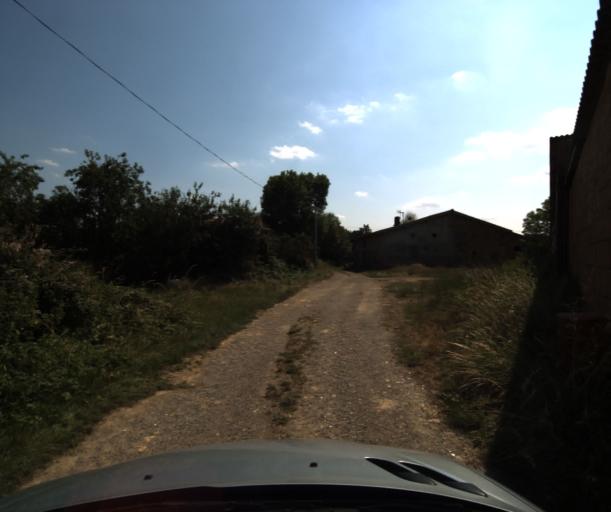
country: FR
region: Midi-Pyrenees
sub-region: Departement de la Haute-Garonne
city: Saint-Lys
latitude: 43.5082
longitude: 1.1605
